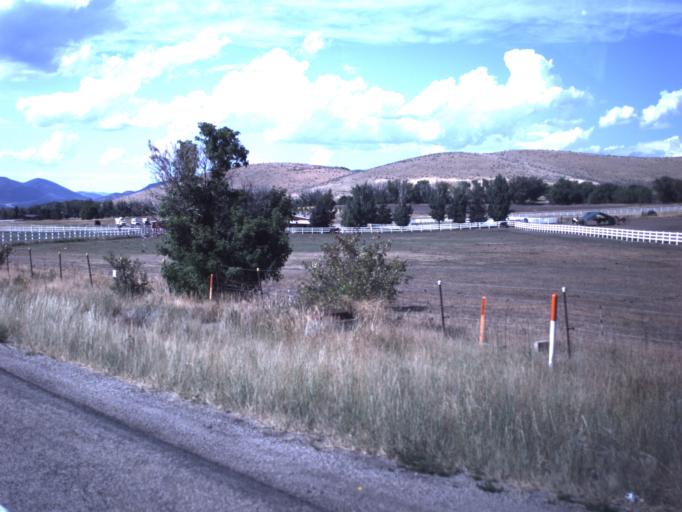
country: US
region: Utah
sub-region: Wasatch County
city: Heber
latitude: 40.4562
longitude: -111.3758
